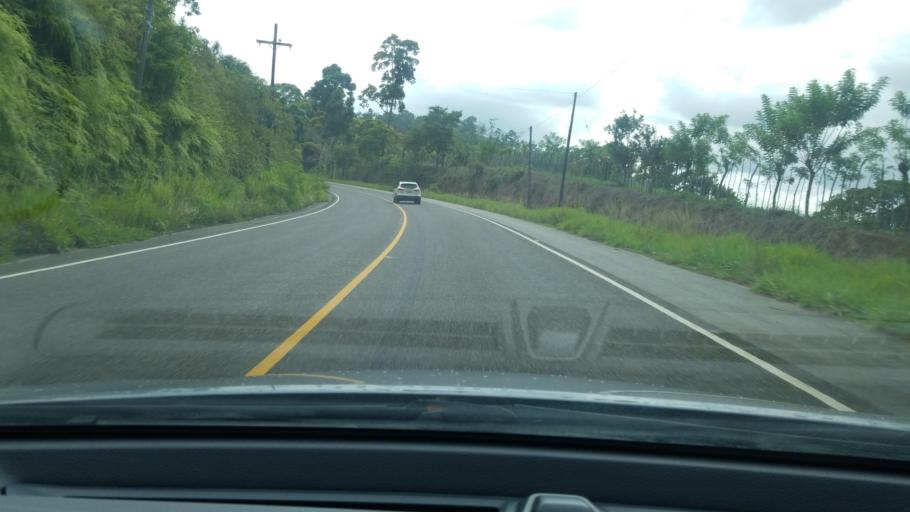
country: HN
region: Cortes
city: Potrerillos
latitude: 15.6098
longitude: -88.2891
